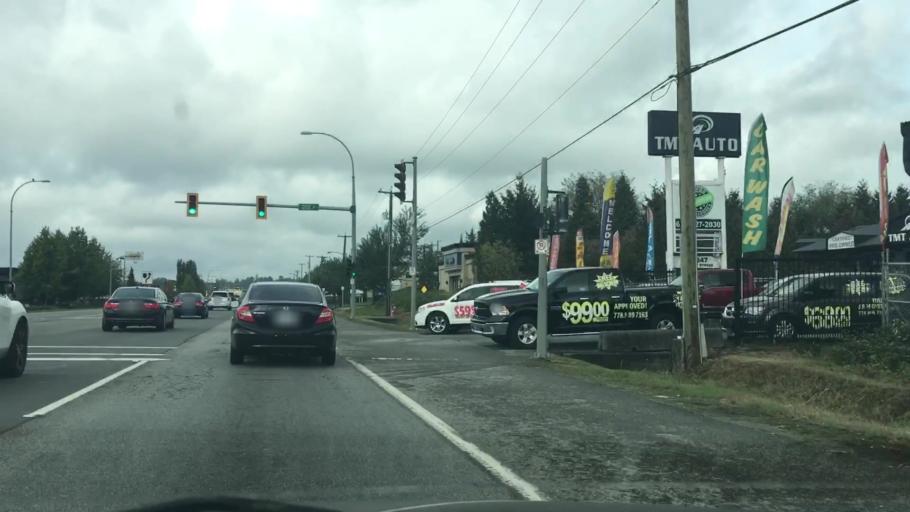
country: CA
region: British Columbia
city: Langley
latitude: 49.1134
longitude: -122.6618
